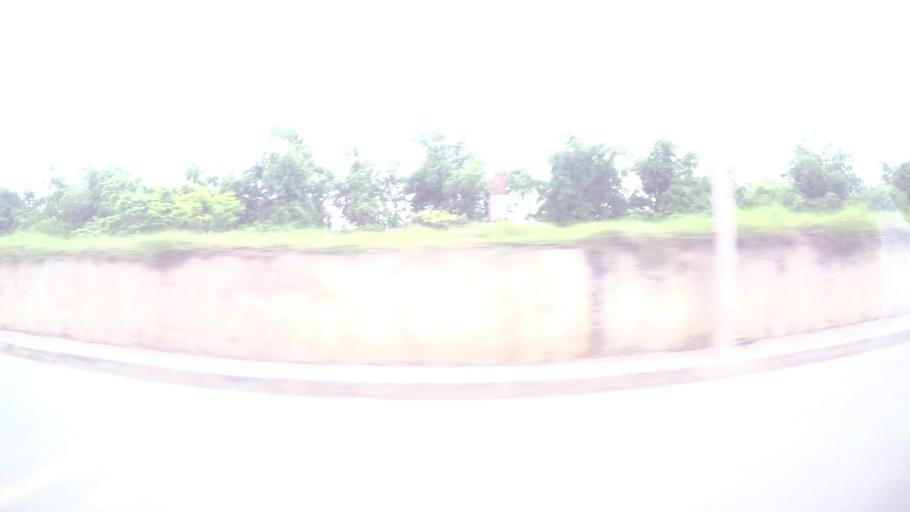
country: VN
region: Ha Noi
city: Trau Quy
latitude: 21.0618
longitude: 105.9201
